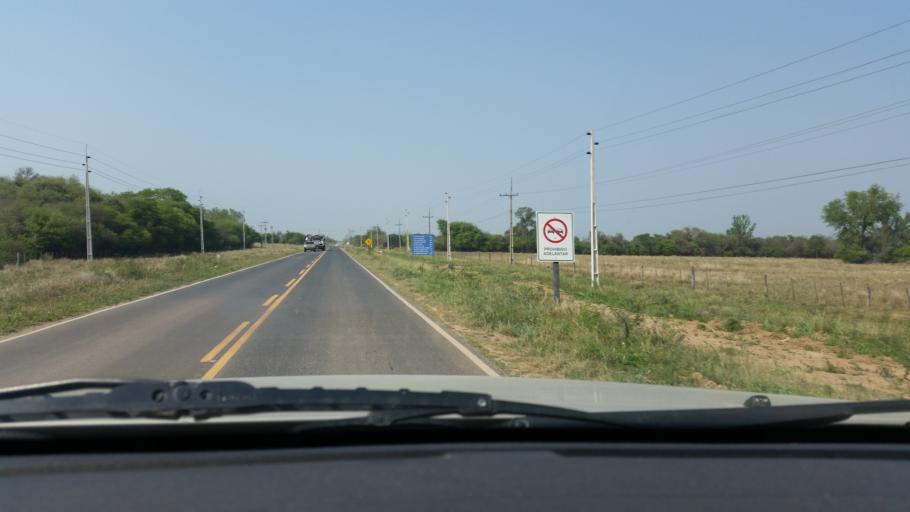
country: PY
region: Boqueron
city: Filadelfia
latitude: -22.4086
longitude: -60.0351
